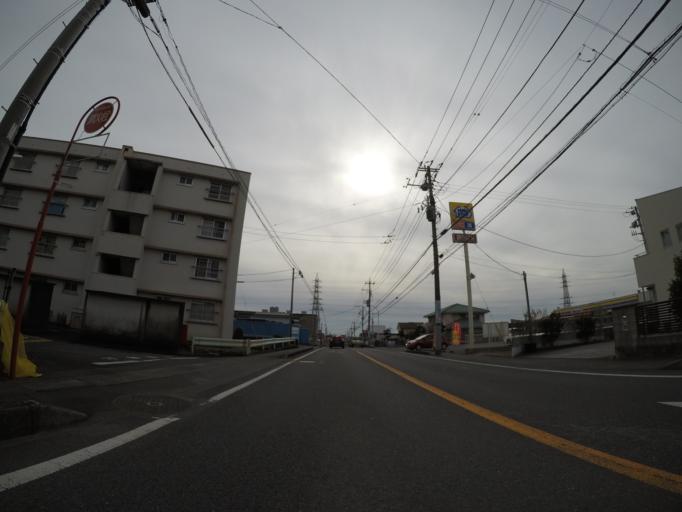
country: JP
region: Shizuoka
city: Fuji
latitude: 35.1762
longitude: 138.6826
